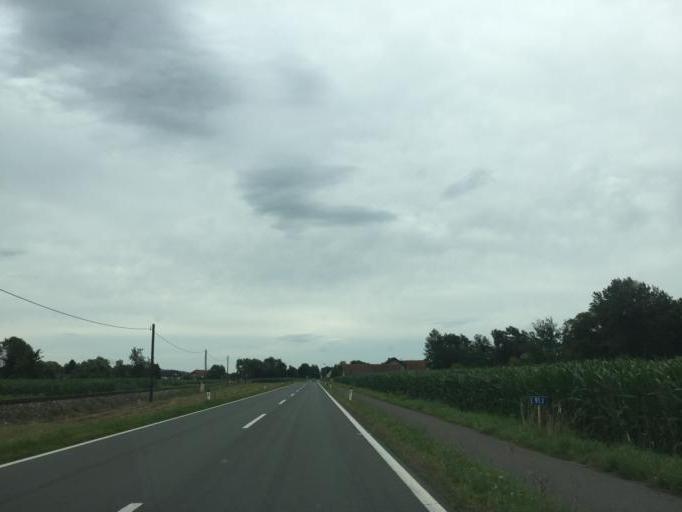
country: AT
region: Styria
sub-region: Politischer Bezirk Suedoststeiermark
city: Ratschendorf
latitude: 46.7281
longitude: 15.8248
